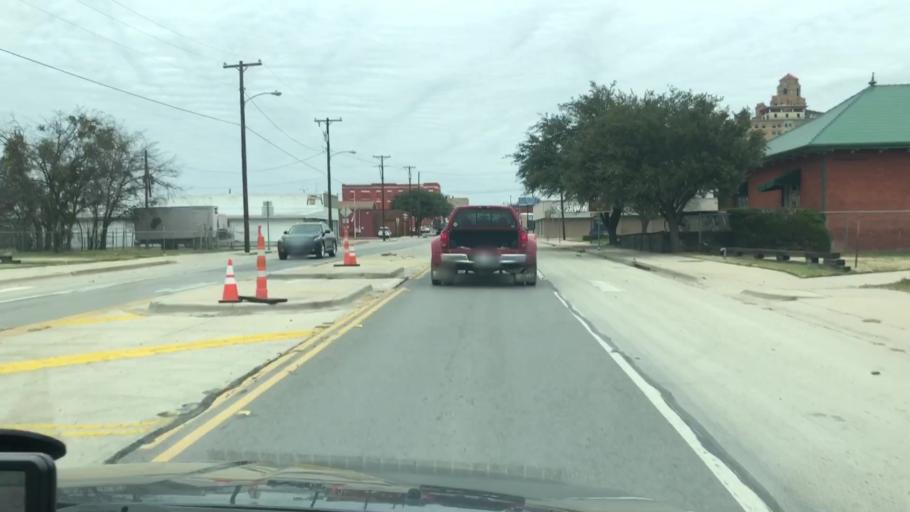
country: US
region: Texas
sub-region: Palo Pinto County
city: Mineral Wells
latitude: 32.8062
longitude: -98.1129
